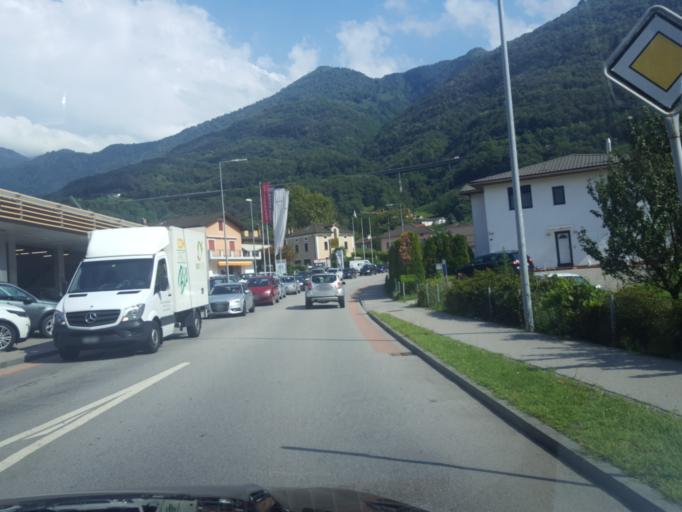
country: CH
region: Ticino
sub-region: Bellinzona District
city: Cadenazzo
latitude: 46.1518
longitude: 8.9469
